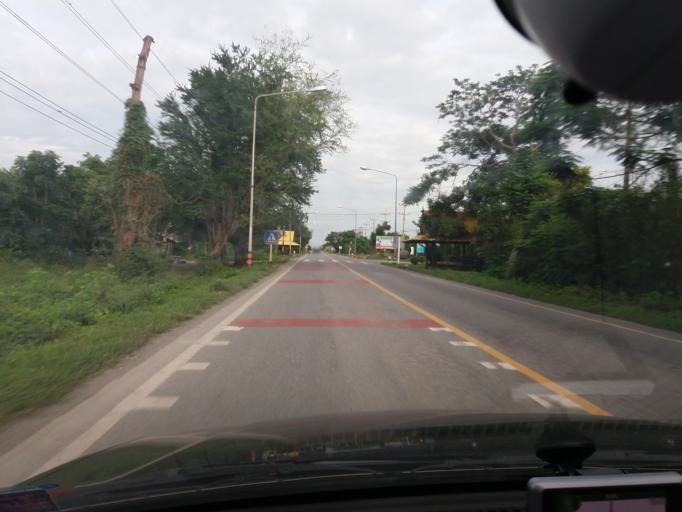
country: TH
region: Suphan Buri
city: U Thong
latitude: 14.3359
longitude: 99.8033
